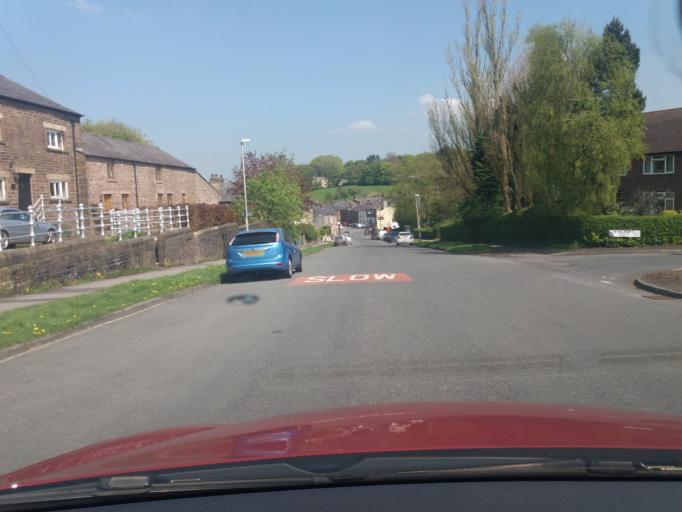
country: GB
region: England
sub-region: Lancashire
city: Chorley
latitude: 53.6841
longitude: -2.6082
